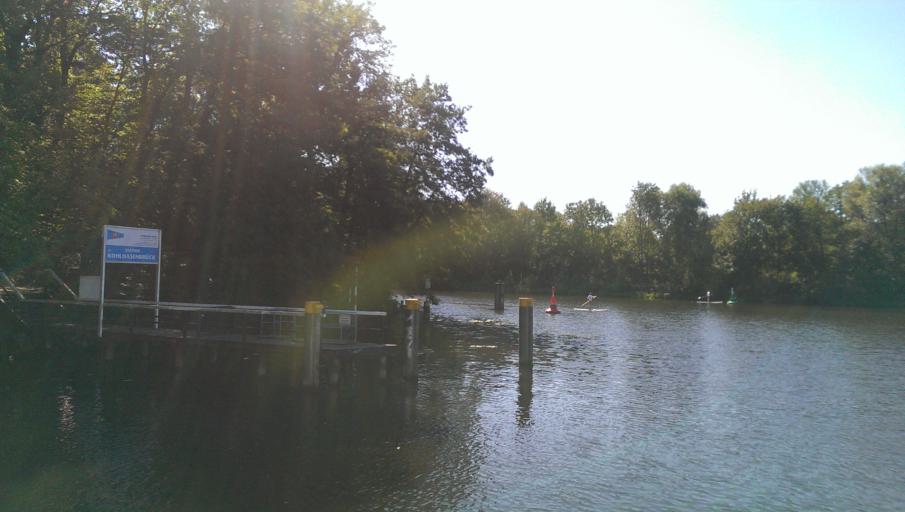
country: DE
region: Berlin
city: Wannsee
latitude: 52.4018
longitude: 13.1395
